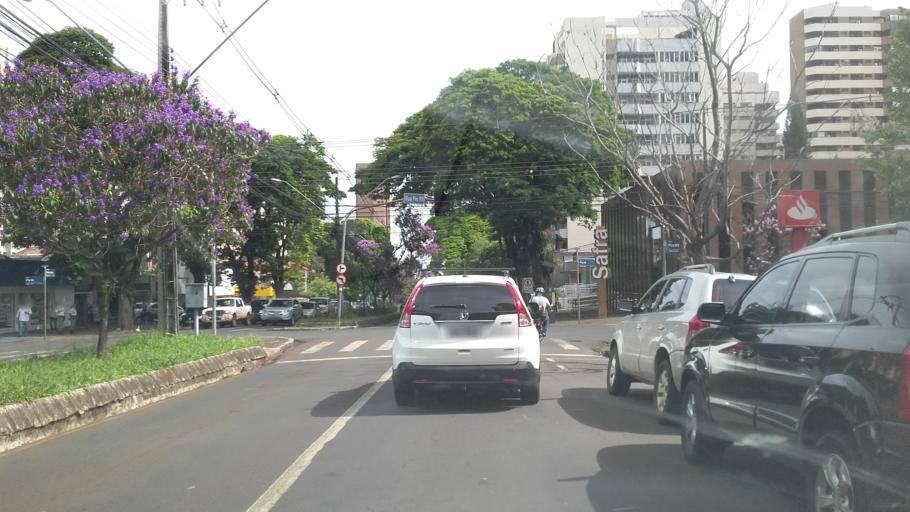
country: BR
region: Parana
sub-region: Londrina
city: Londrina
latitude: -23.3118
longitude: -51.1656
